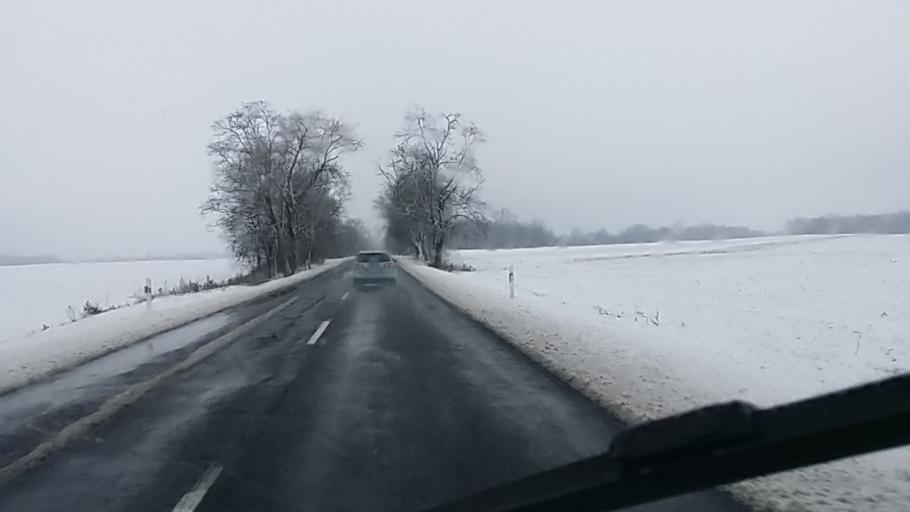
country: HU
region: Komarom-Esztergom
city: Acs
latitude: 47.7342
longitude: 17.9747
